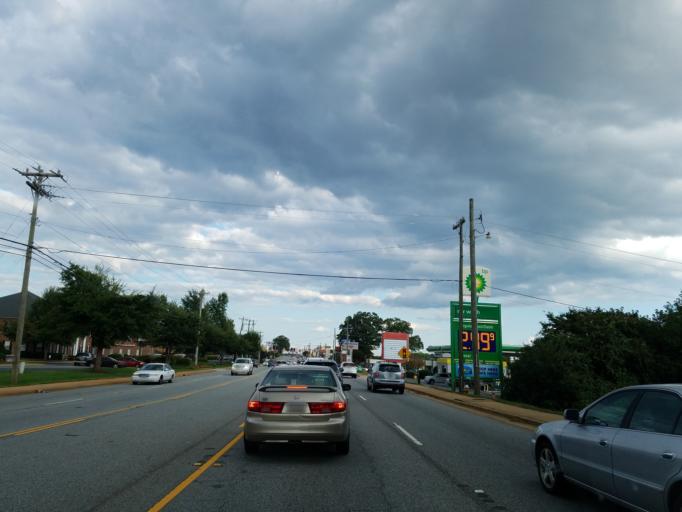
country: US
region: South Carolina
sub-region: Greenville County
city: Taylors
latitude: 34.8608
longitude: -82.2726
